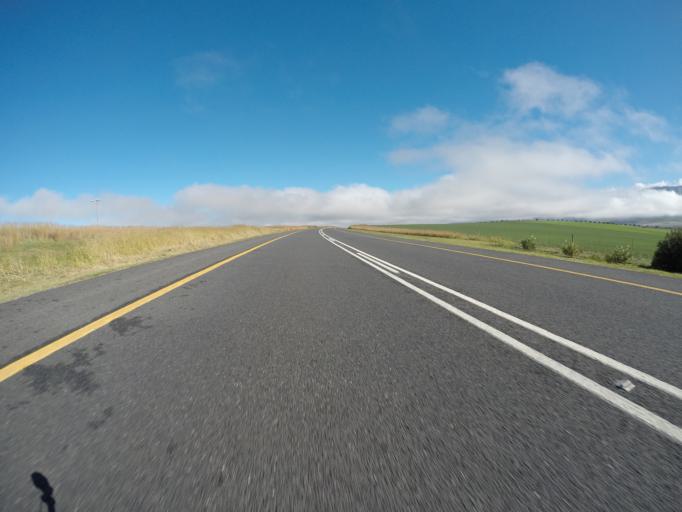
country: ZA
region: Western Cape
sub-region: Cape Winelands District Municipality
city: Ashton
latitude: -34.1398
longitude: 20.0219
